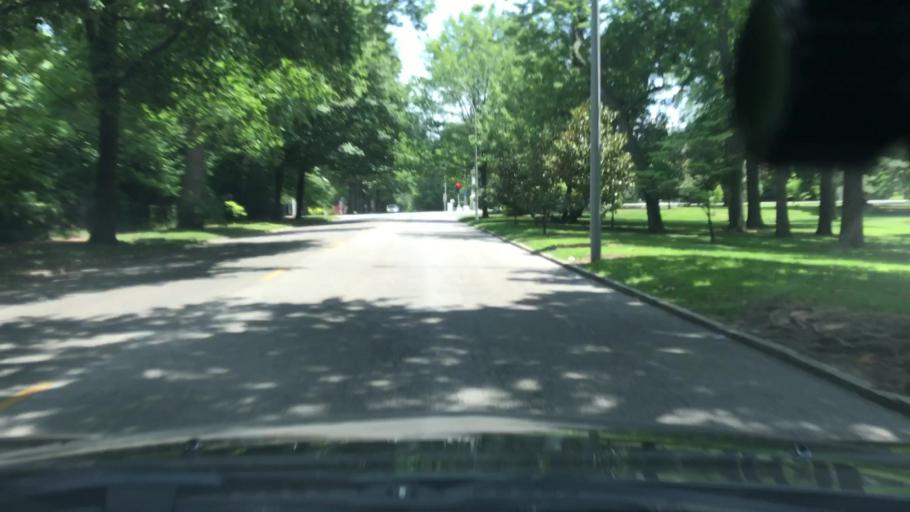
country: US
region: Missouri
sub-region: Saint Louis County
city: Richmond Heights
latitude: 38.6089
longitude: -90.2592
